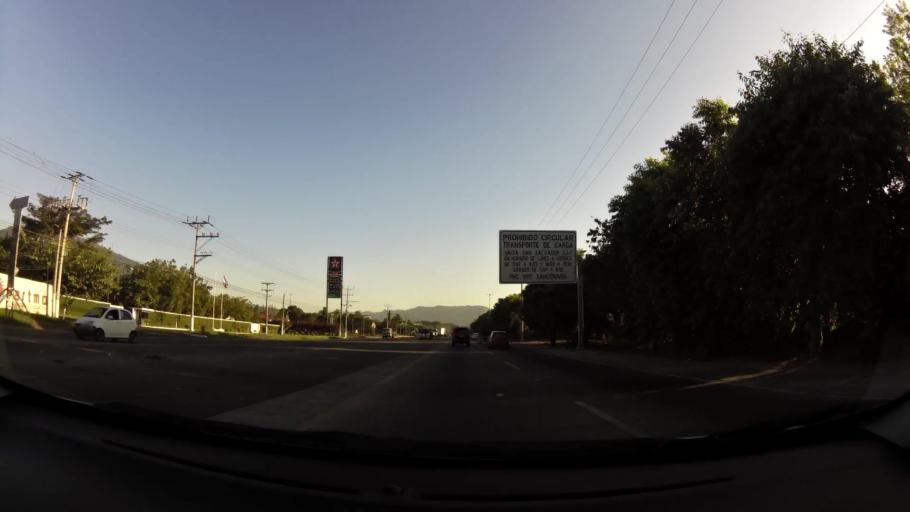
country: SV
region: La Libertad
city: Ciudad Arce
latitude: 13.7658
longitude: -89.3698
